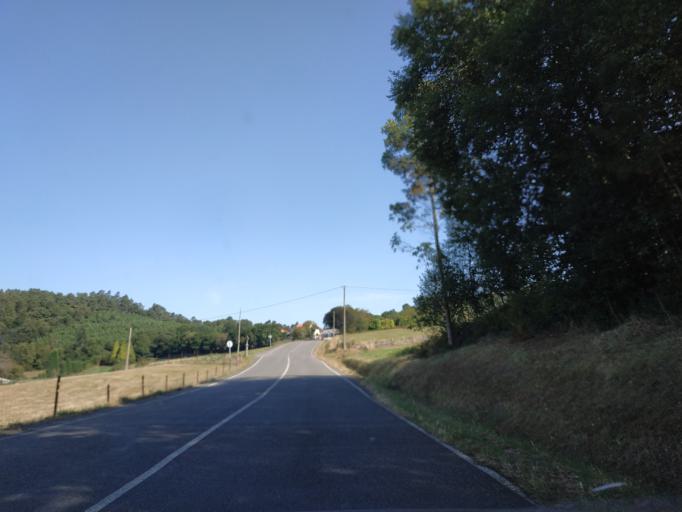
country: ES
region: Galicia
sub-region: Provincia da Coruna
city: Laracha
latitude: 43.2266
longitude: -8.5463
